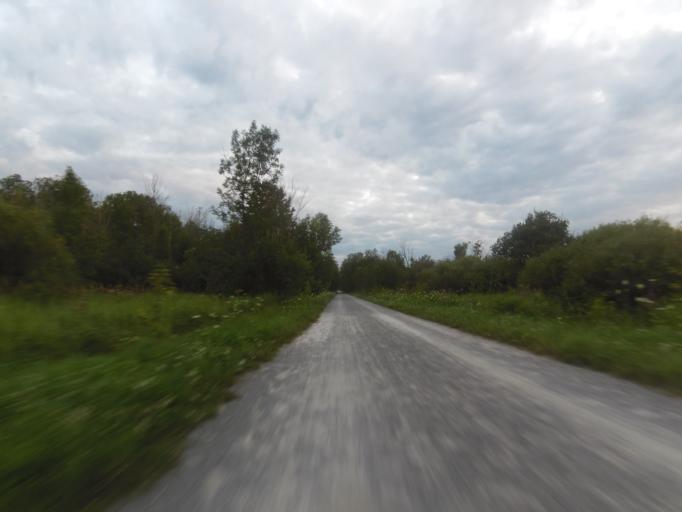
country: CA
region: Ontario
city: Bells Corners
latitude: 45.2513
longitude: -75.9317
